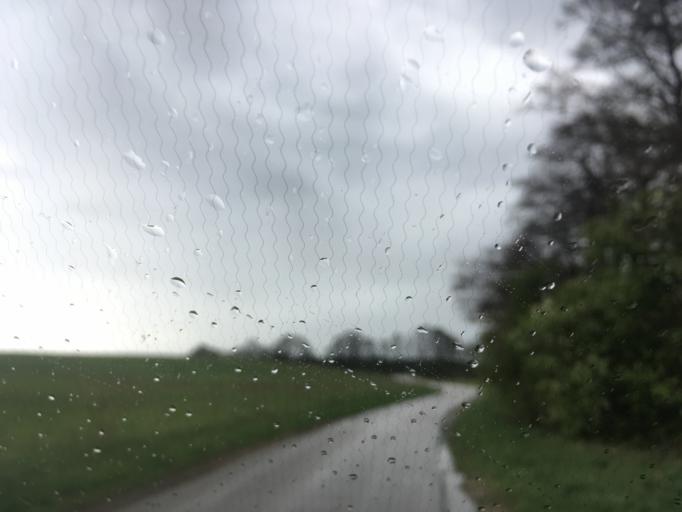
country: PL
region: Warmian-Masurian Voivodeship
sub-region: Powiat dzialdowski
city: Rybno
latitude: 53.3801
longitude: 19.9907
